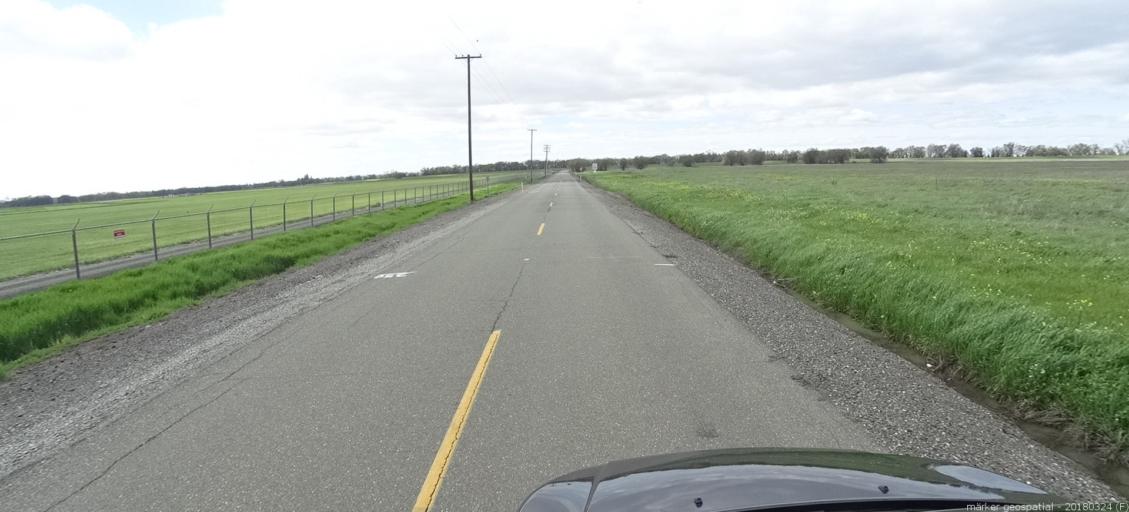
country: US
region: California
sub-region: Sacramento County
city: Elverta
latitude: 38.7144
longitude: -121.5951
